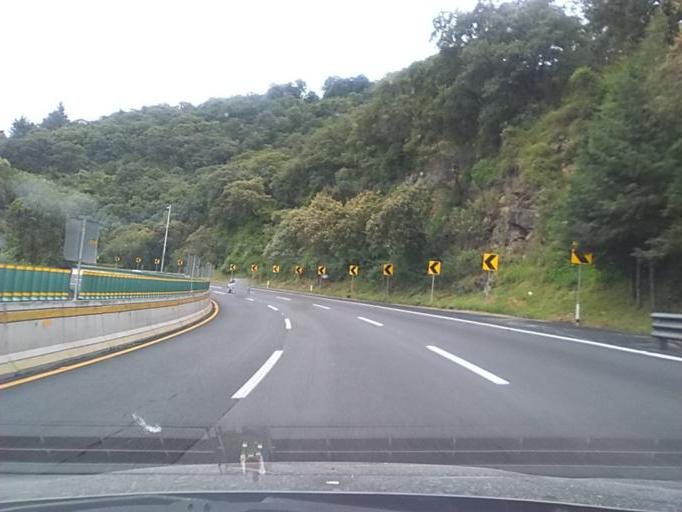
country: MX
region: Mexico City
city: Xochimilco
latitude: 19.2230
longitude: -99.1384
